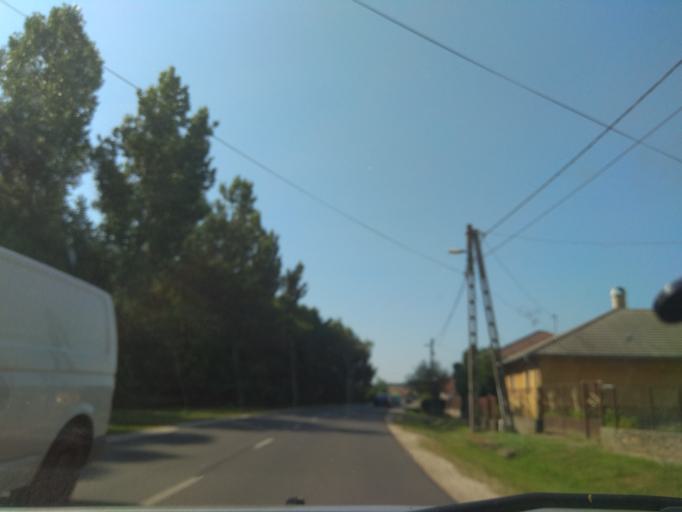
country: HU
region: Borsod-Abauj-Zemplen
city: Harsany
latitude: 47.9789
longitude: 20.7454
